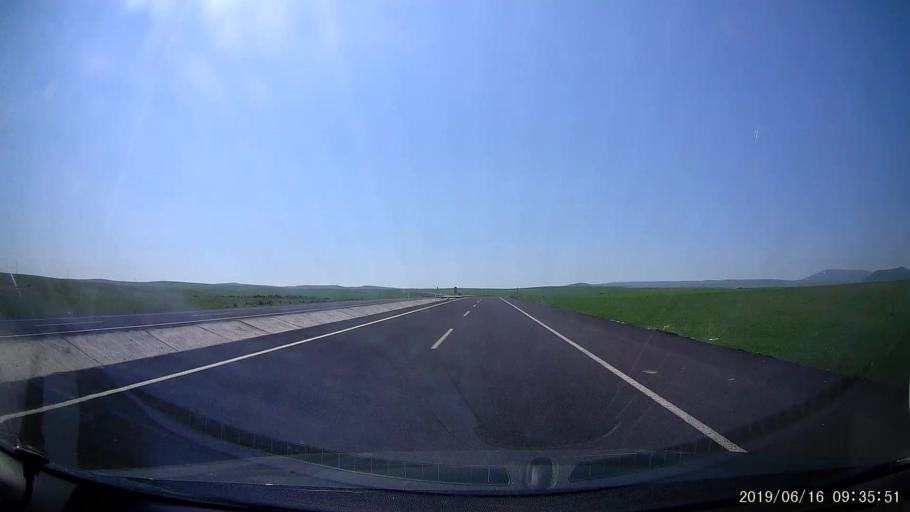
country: TR
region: Kars
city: Kars
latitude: 40.5654
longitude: 43.1629
